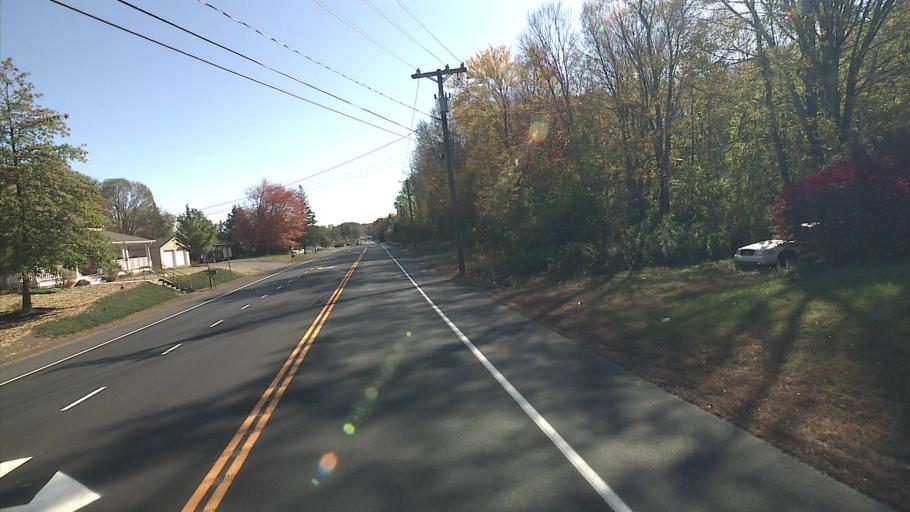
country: US
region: Connecticut
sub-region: Tolland County
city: South Coventry
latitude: 41.7285
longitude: -72.3209
